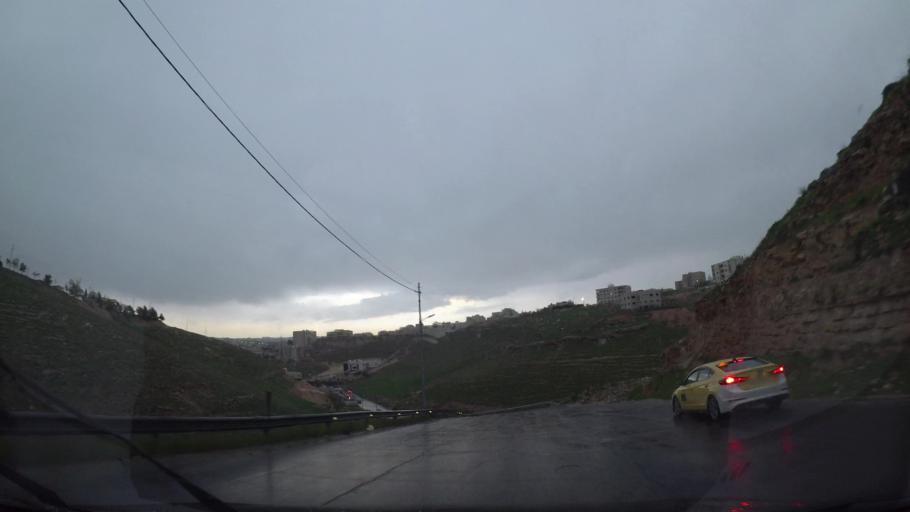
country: JO
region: Amman
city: Amman
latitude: 31.9971
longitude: 35.9695
